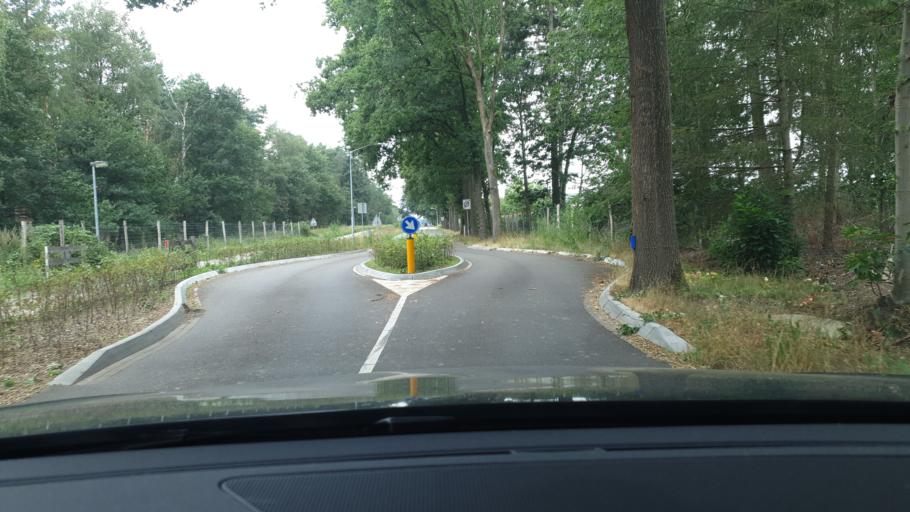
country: NL
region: North Brabant
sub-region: Gemeente Oirschot
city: Oostelbeers
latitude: 51.4484
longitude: 5.3012
